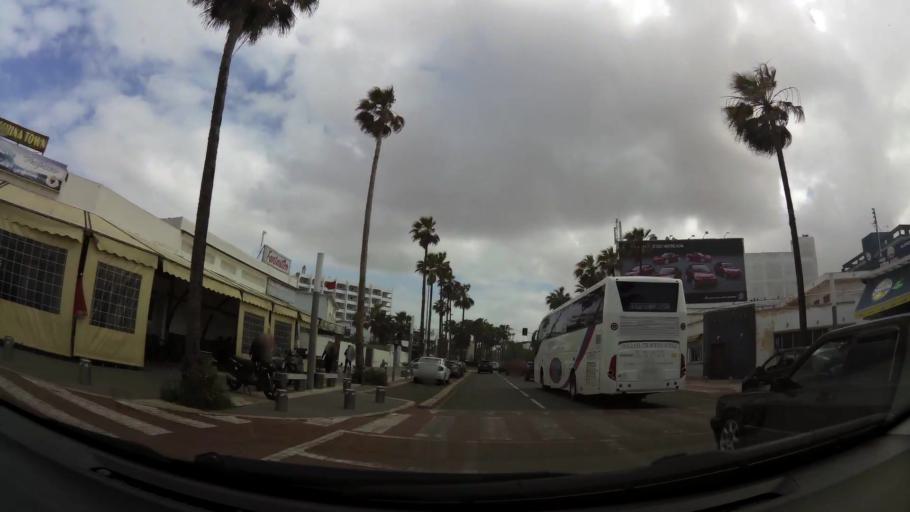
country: MA
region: Grand Casablanca
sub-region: Casablanca
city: Casablanca
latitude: 33.5925
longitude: -7.6779
